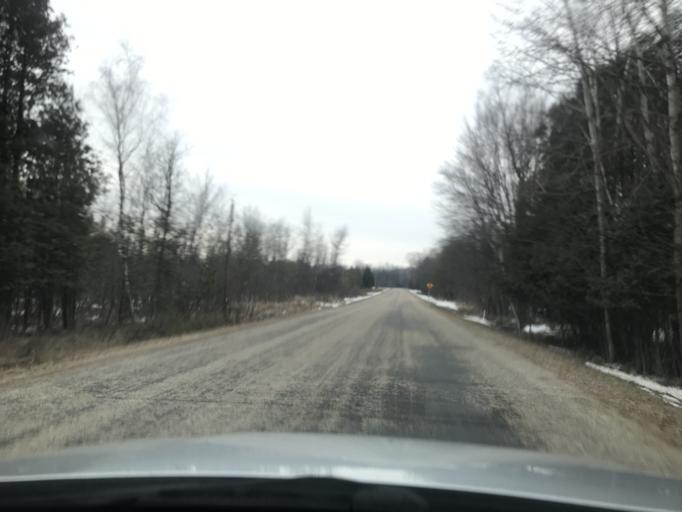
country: US
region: Wisconsin
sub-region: Marinette County
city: Peshtigo
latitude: 45.0899
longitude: -87.9324
